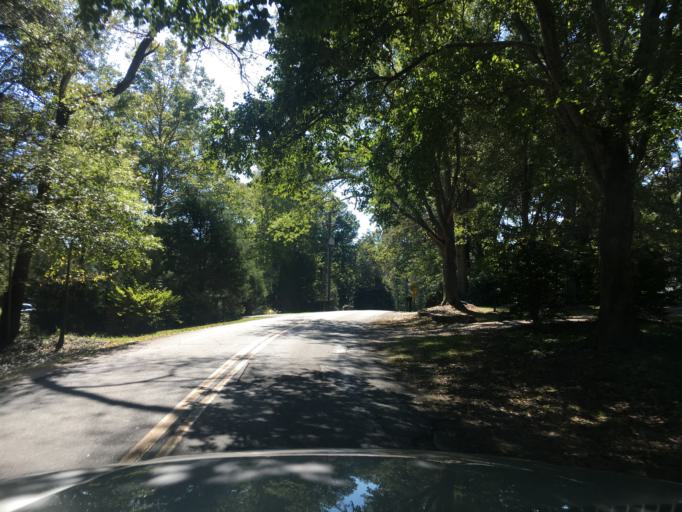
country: US
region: South Carolina
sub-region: Greenville County
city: Taylors
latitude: 34.8994
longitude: -82.2730
